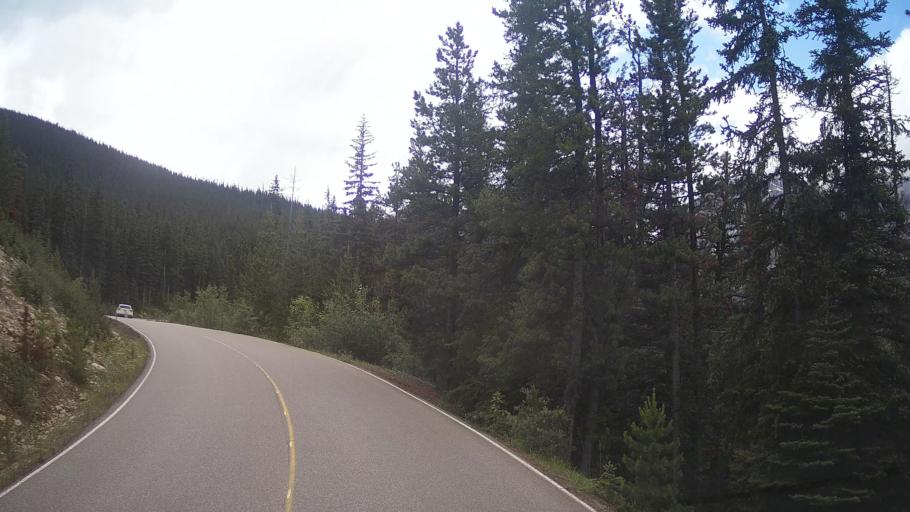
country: CA
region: Alberta
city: Jasper Park Lodge
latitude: 52.7152
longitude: -118.0556
